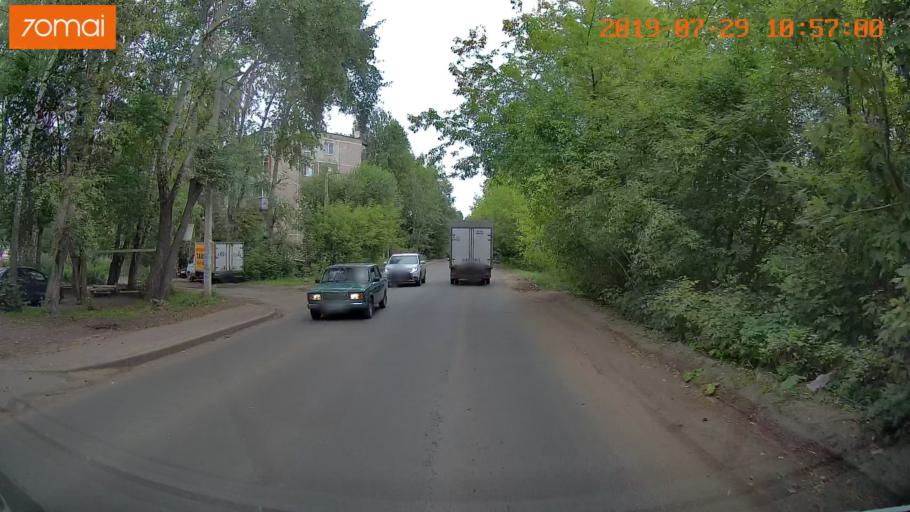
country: RU
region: Ivanovo
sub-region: Gorod Ivanovo
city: Ivanovo
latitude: 56.9864
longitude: 41.0339
